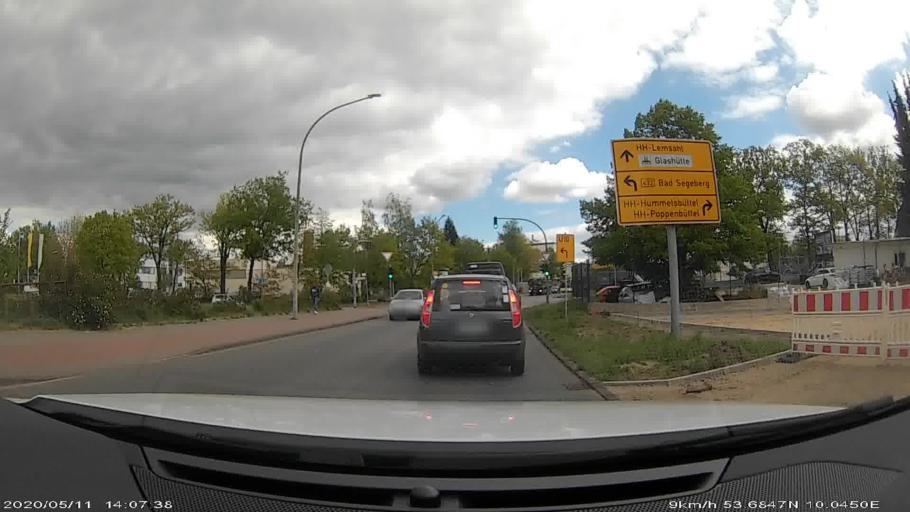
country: DE
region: Hamburg
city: Poppenbuettel
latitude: 53.6839
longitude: 10.0642
